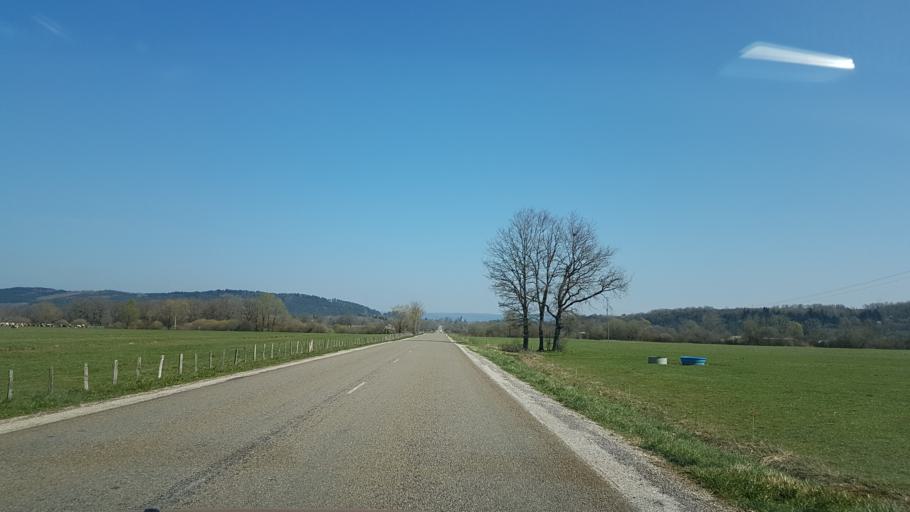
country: FR
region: Franche-Comte
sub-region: Departement du Jura
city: Orgelet
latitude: 46.5254
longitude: 5.5715
